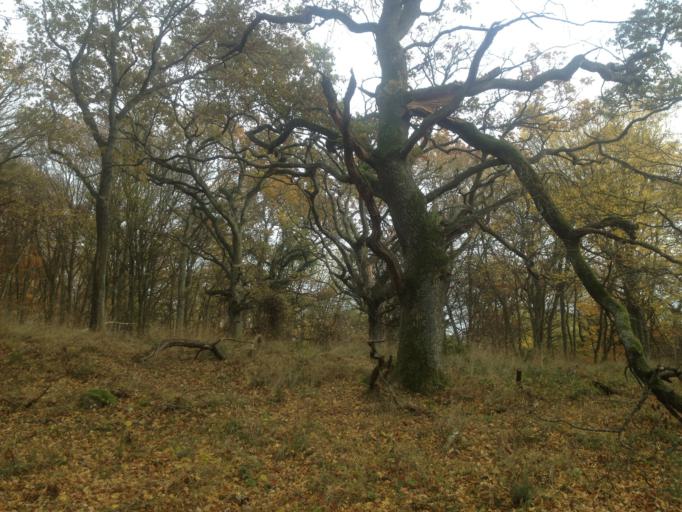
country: SE
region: Skane
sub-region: Simrishamns Kommun
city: Kivik
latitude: 55.6605
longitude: 14.2716
